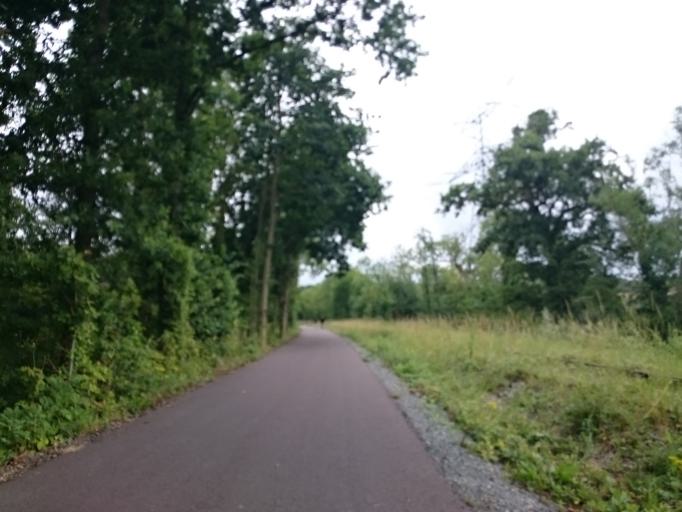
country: FR
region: Lower Normandy
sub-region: Departement du Calvados
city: Saint-Andre-sur-Orne
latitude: 49.1284
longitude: -0.4024
